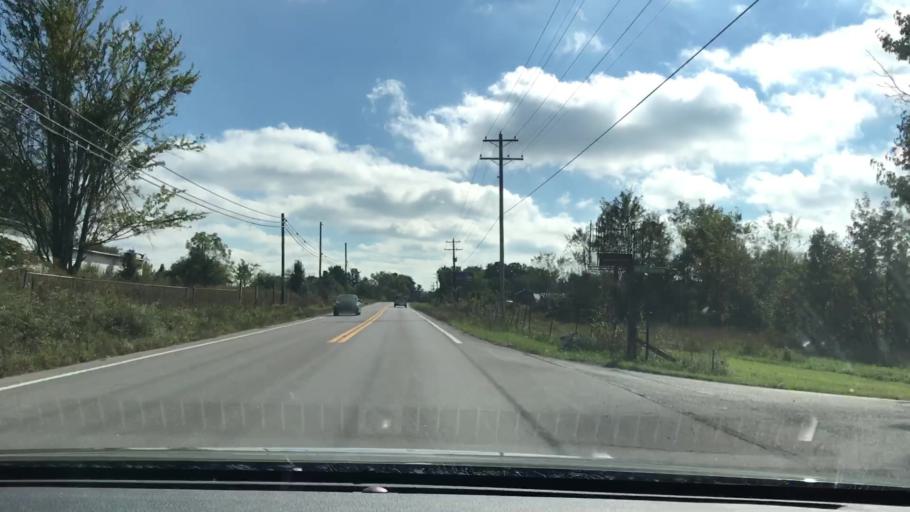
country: US
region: Tennessee
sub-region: Fentress County
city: Grimsley
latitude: 36.2081
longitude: -85.0169
